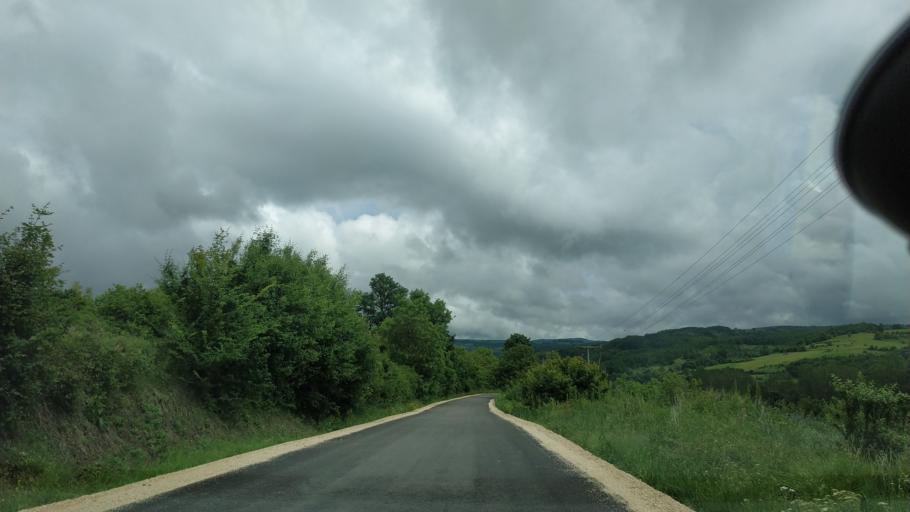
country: RS
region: Central Serbia
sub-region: Zajecarski Okrug
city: Soko Banja
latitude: 43.6519
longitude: 21.9021
